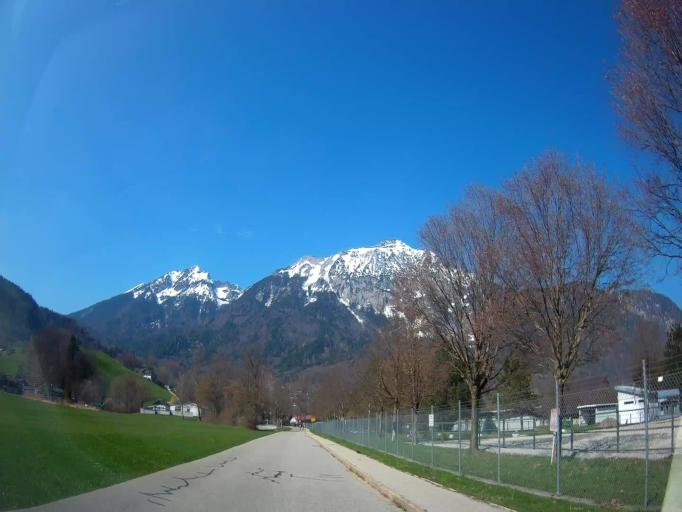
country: DE
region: Bavaria
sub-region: Upper Bavaria
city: Bad Reichenhall
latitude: 47.7237
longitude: 12.8581
